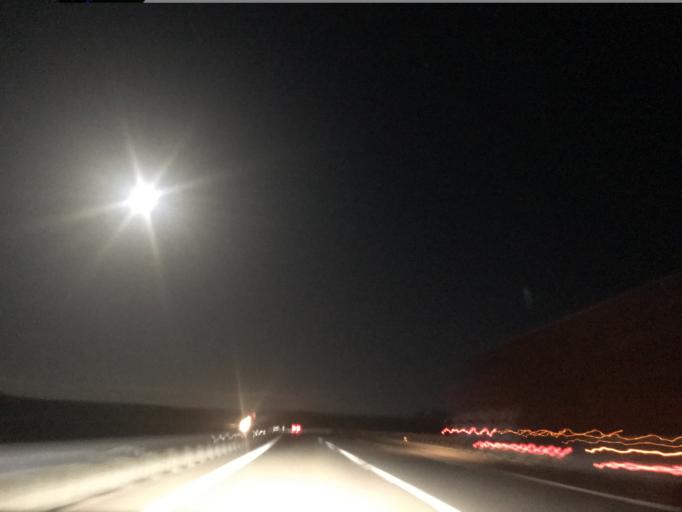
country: TR
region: Nigde
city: Ulukisla
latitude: 37.6407
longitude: 34.3829
